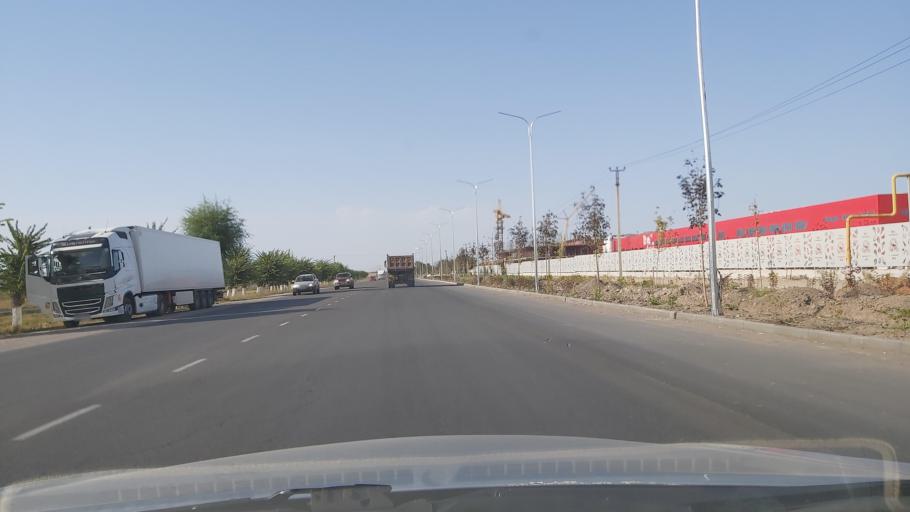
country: KZ
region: Almaty Oblysy
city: Energeticheskiy
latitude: 43.4577
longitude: 77.0339
